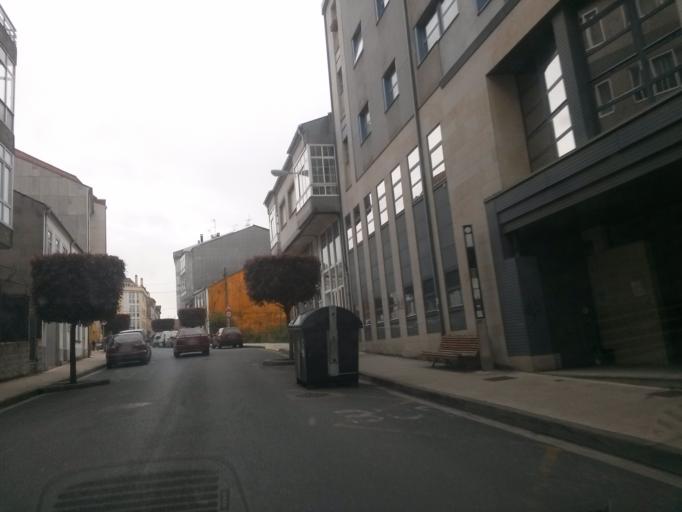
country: ES
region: Galicia
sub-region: Provincia de Lugo
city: Lugo
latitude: 43.0262
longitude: -7.5632
